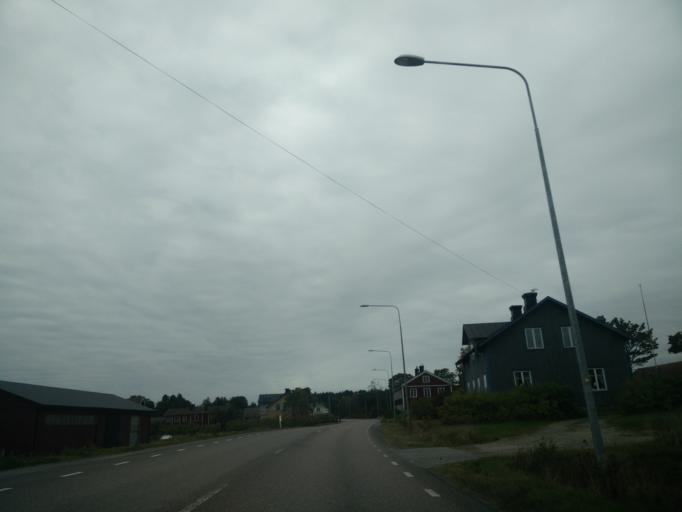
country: SE
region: Gaevleborg
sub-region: Gavle Kommun
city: Norrsundet
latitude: 60.8200
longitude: 17.2119
